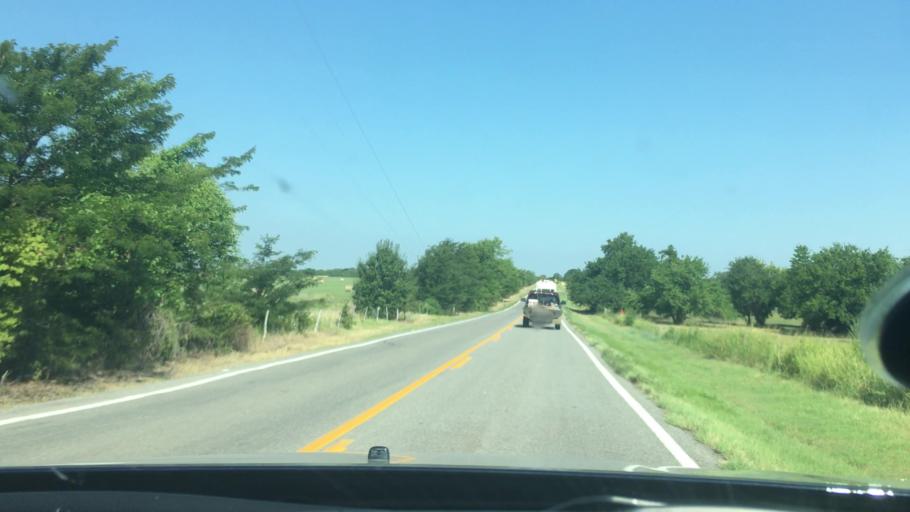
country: US
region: Oklahoma
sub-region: Johnston County
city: Tishomingo
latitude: 34.1946
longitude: -96.5366
